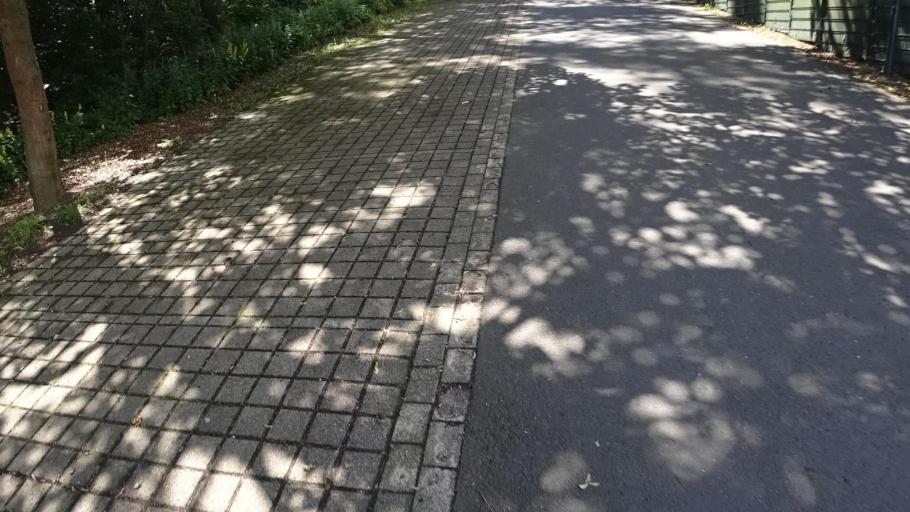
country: DE
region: Rheinland-Pfalz
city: Vettelschoss
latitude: 50.6203
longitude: 7.3418
